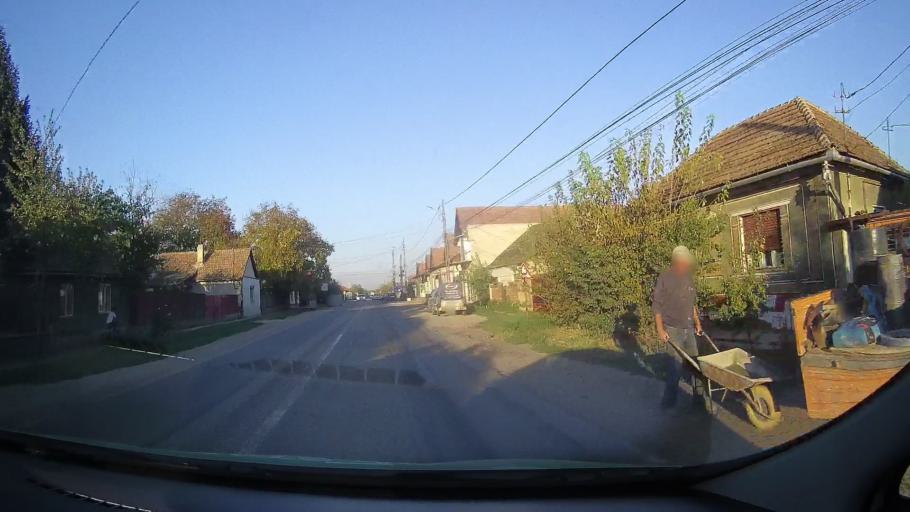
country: RO
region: Bihor
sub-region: Comuna Salard
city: Salard
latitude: 47.2165
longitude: 22.0312
